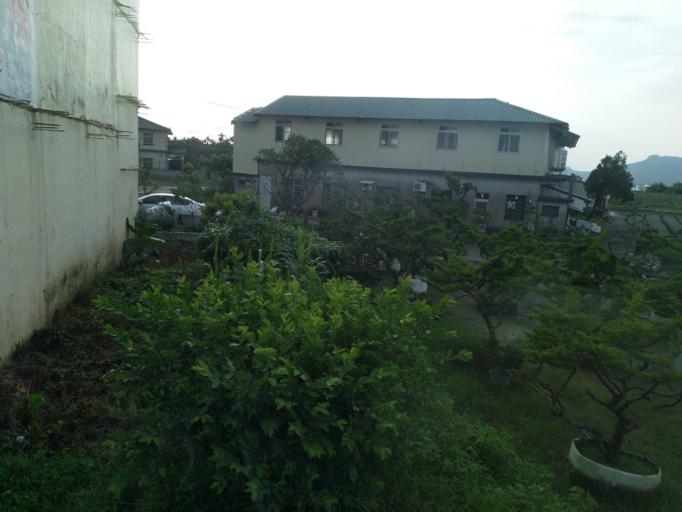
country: TW
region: Taiwan
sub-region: Pingtung
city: Pingtung
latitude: 22.8752
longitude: 120.5361
